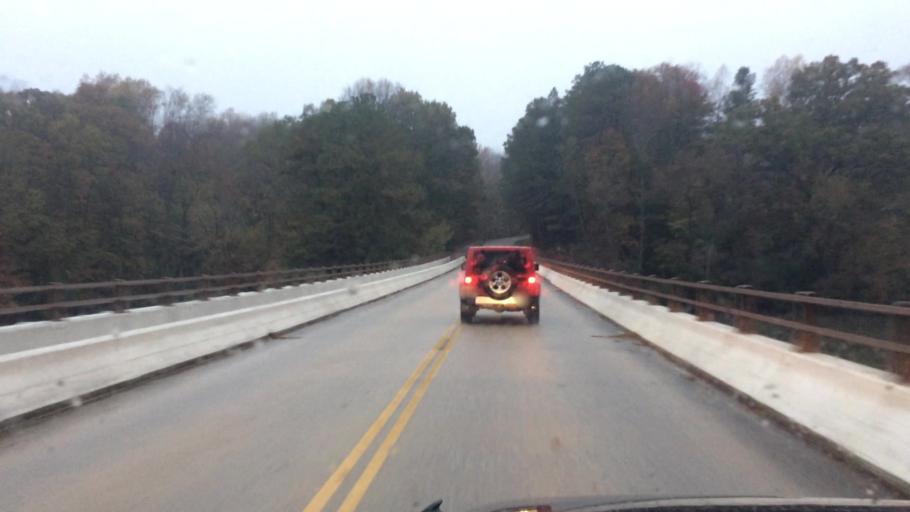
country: US
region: Virginia
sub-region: City of Williamsburg
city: Williamsburg
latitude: 37.2359
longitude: -76.6805
